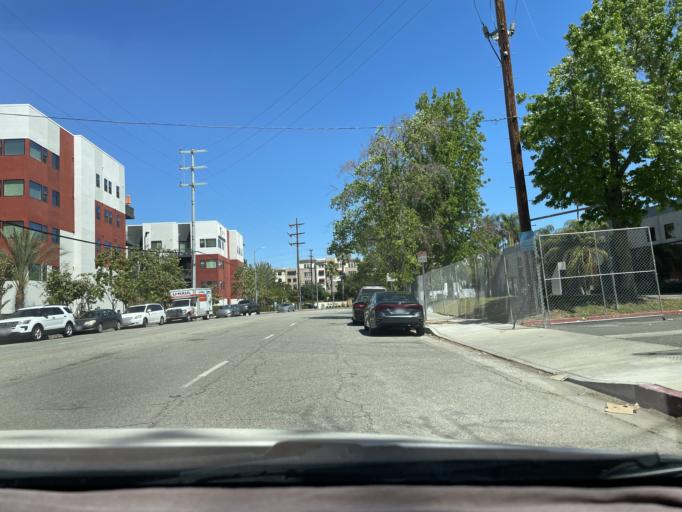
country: US
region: California
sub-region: Los Angeles County
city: Canoga Park
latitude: 34.1828
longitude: -118.5918
